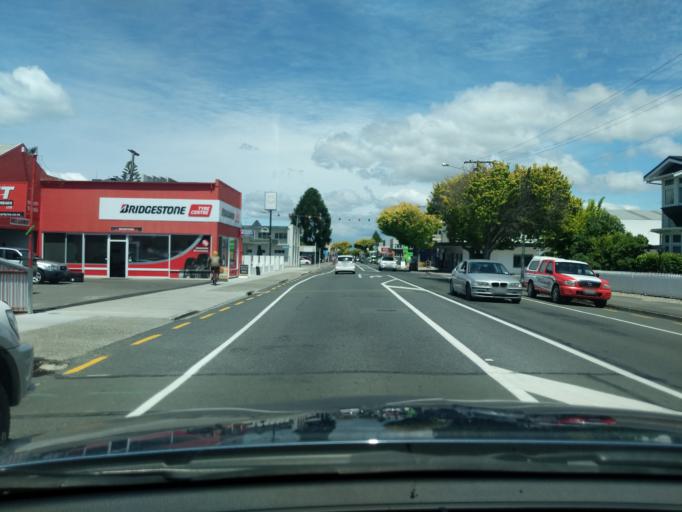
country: NZ
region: Tasman
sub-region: Tasman District
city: Motueka
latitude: -41.1076
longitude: 173.0113
